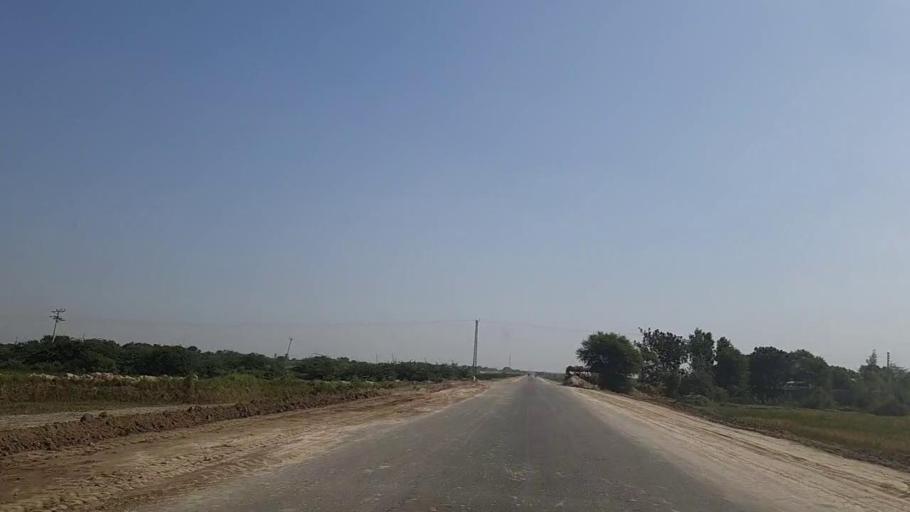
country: PK
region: Sindh
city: Mirpur Batoro
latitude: 24.7506
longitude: 68.2355
